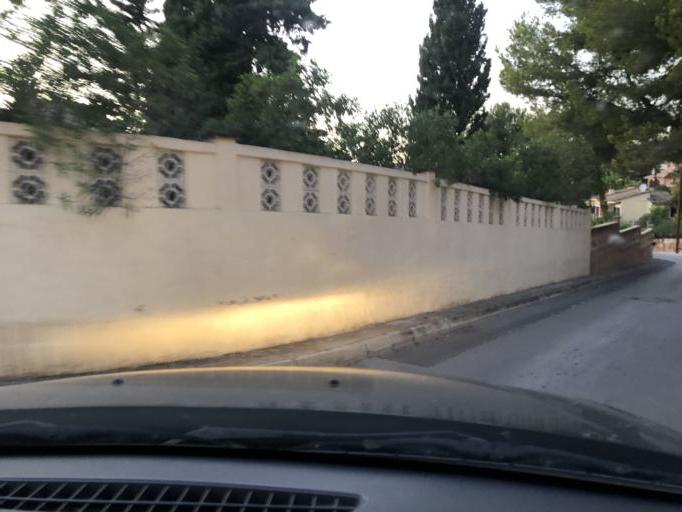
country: ES
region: Balearic Islands
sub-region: Illes Balears
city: Santa Ponsa
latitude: 39.5247
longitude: 2.4853
